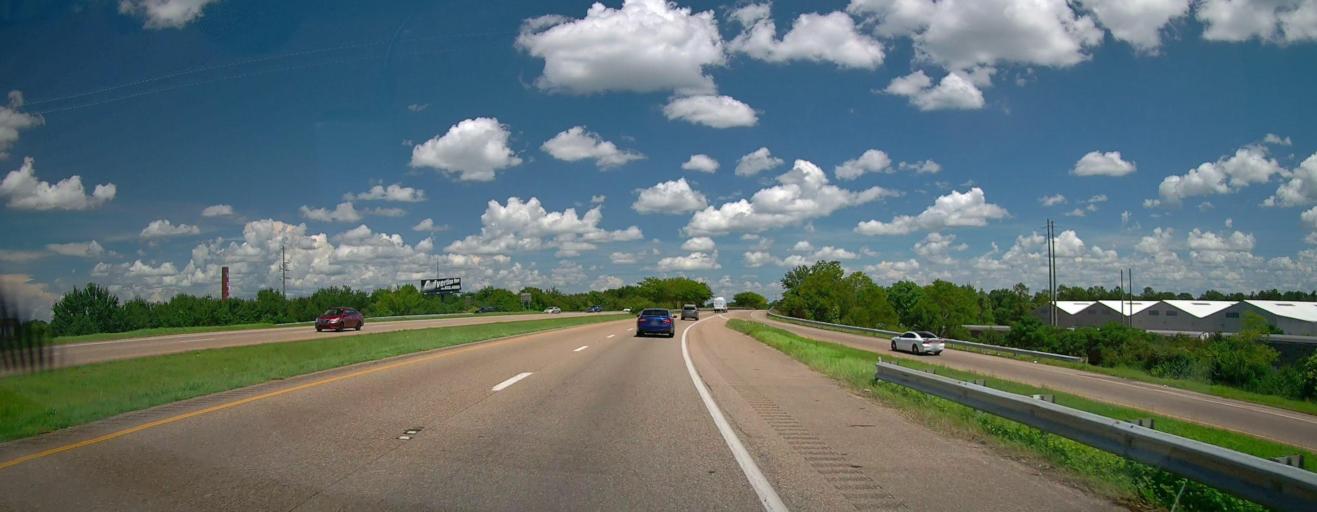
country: US
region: Alabama
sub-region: Montgomery County
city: Montgomery
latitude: 32.4243
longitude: -86.2830
